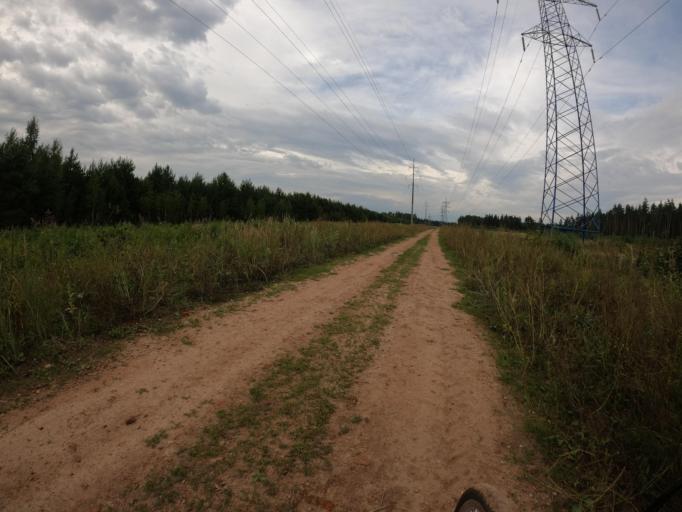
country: RU
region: Moskovskaya
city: Rodniki
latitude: 55.6749
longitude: 38.0840
